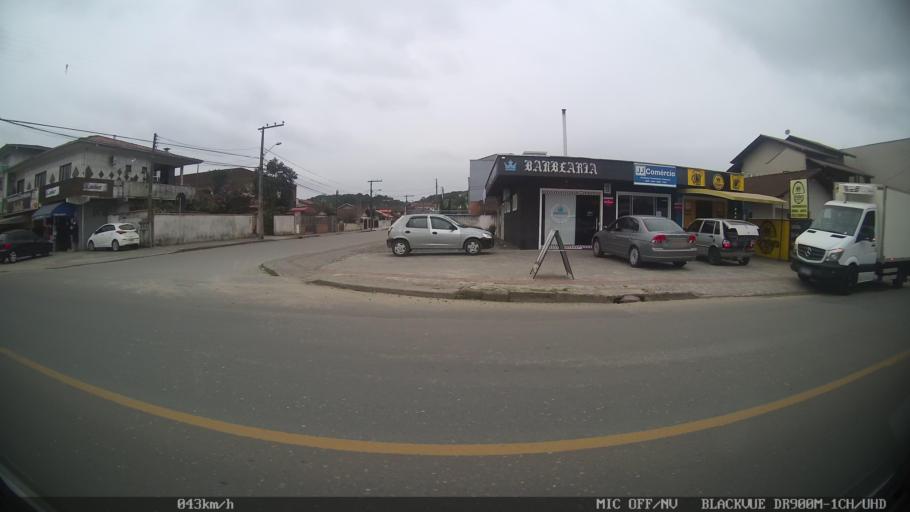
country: BR
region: Santa Catarina
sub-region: Joinville
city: Joinville
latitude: -26.3658
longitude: -48.8295
